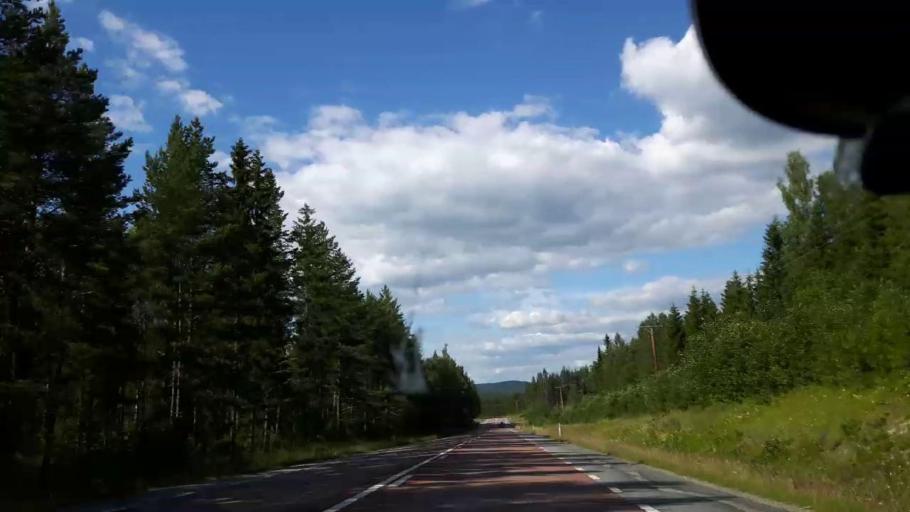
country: SE
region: Jaemtland
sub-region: Braecke Kommun
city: Braecke
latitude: 62.8029
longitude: 15.3704
